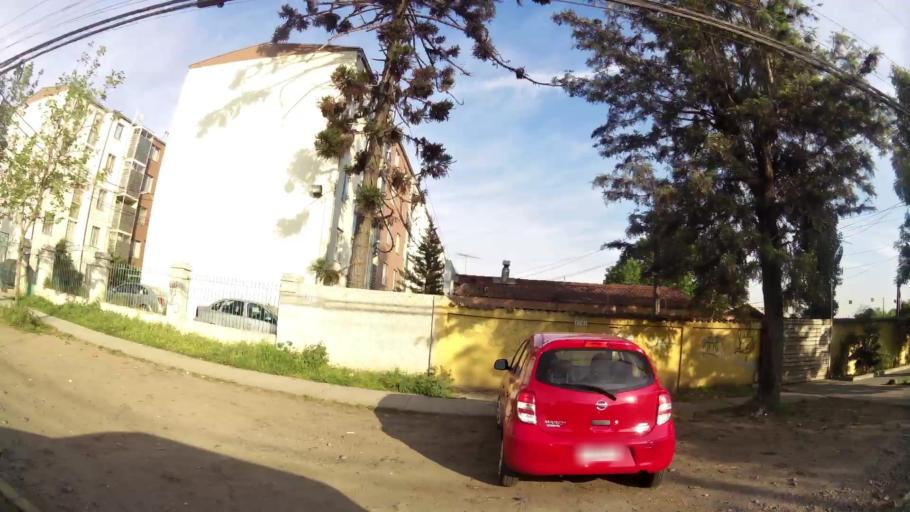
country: CL
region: Santiago Metropolitan
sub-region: Provincia de Santiago
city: La Pintana
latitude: -33.5266
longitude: -70.6712
